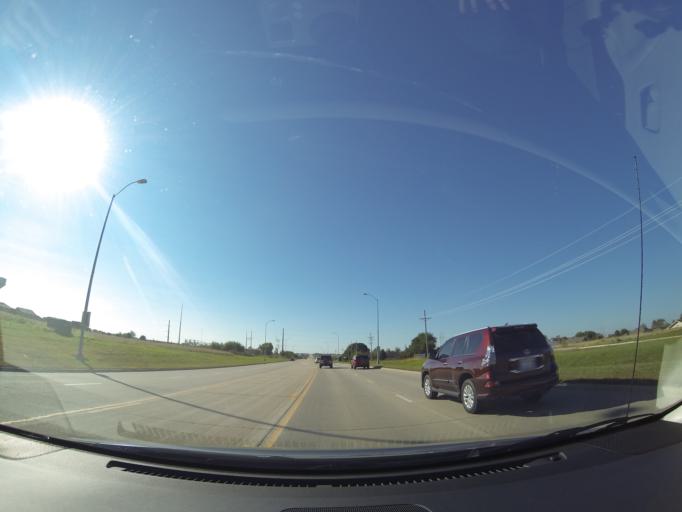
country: US
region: Nebraska
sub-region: Sarpy County
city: Gretna
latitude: 41.1273
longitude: -96.2533
